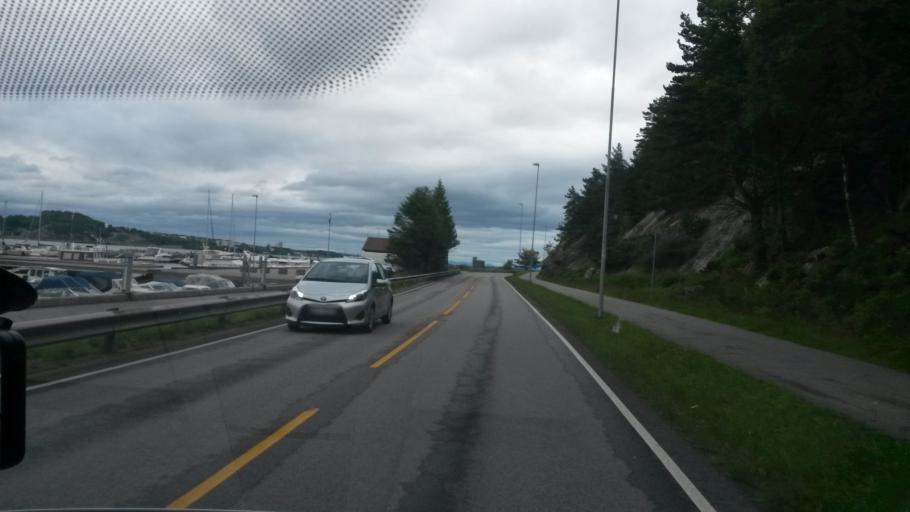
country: NO
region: Rogaland
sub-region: Sandnes
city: Sandnes
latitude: 58.8648
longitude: 5.7562
